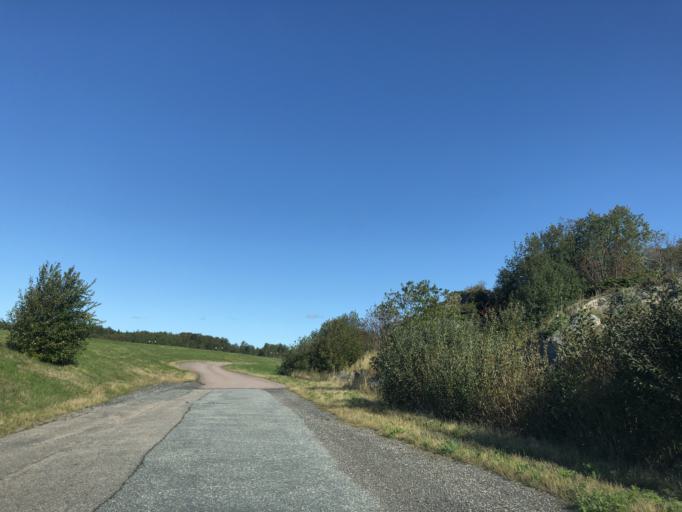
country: SE
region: Vaestra Goetaland
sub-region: Goteborg
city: Torslanda
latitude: 57.7141
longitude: 11.8063
